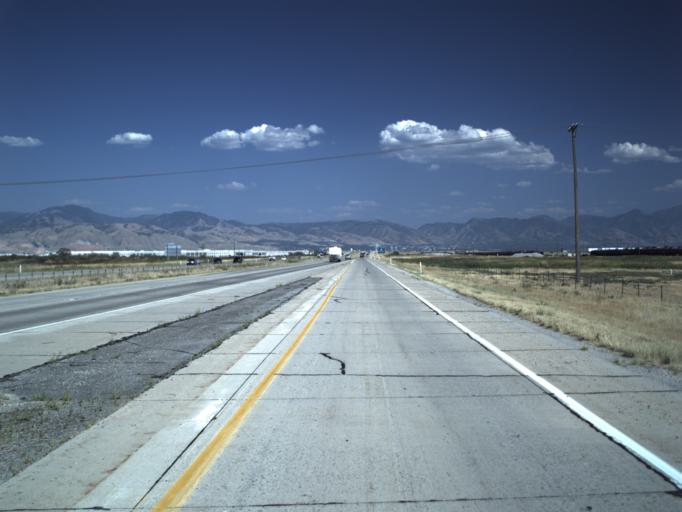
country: US
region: Utah
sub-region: Salt Lake County
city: Magna
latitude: 40.7708
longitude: -112.0578
